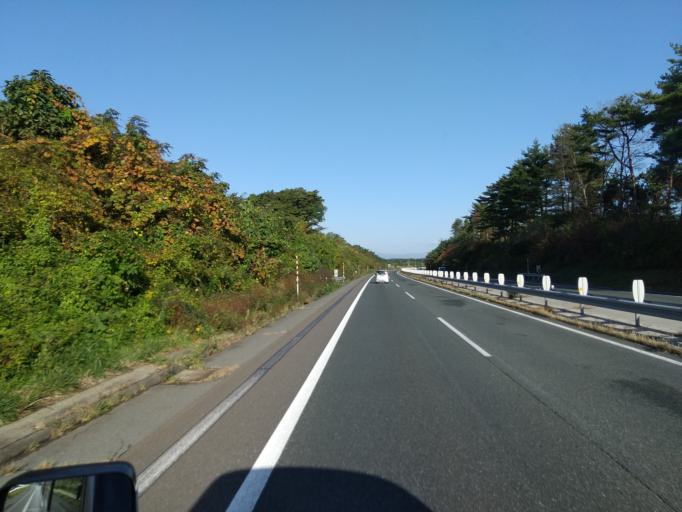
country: JP
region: Iwate
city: Mizusawa
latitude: 39.0664
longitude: 141.1024
